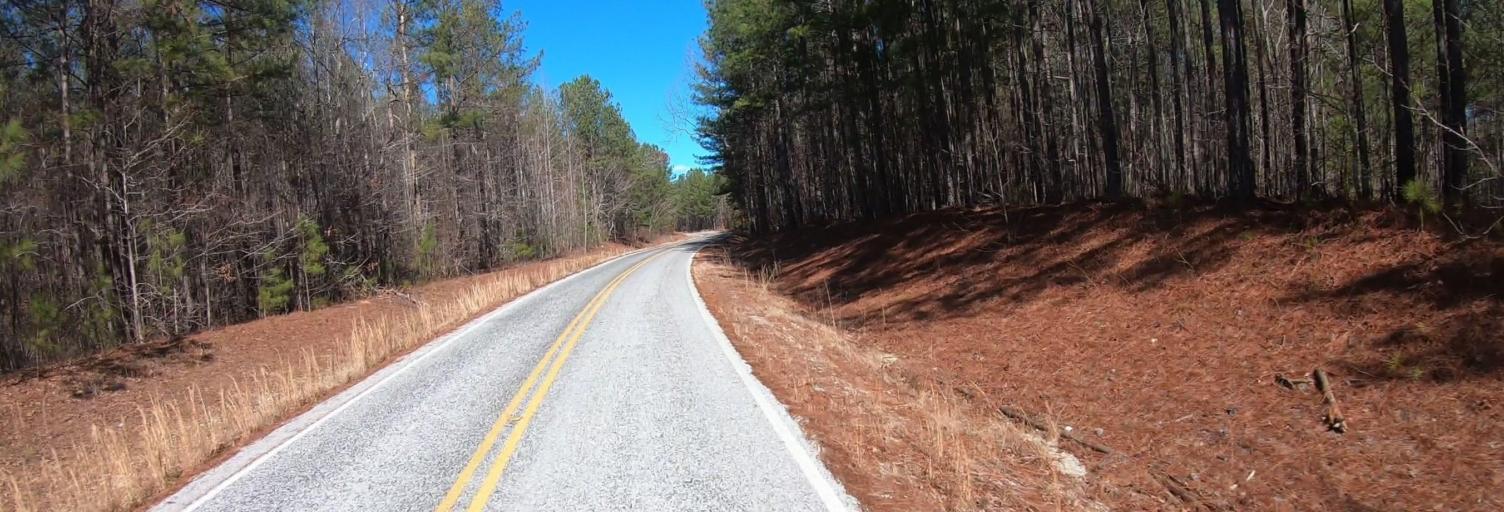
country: US
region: Alabama
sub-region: Clay County
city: Ashland
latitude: 33.3901
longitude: -85.8696
